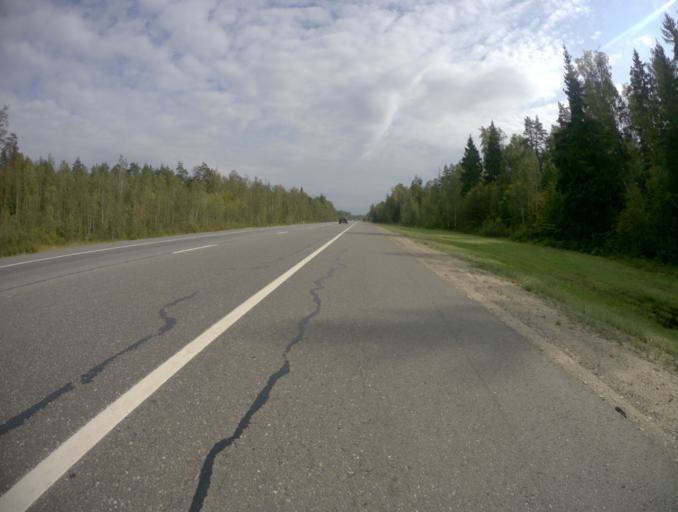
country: RU
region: Vladimir
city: Raduzhnyy
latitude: 56.0700
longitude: 40.2914
